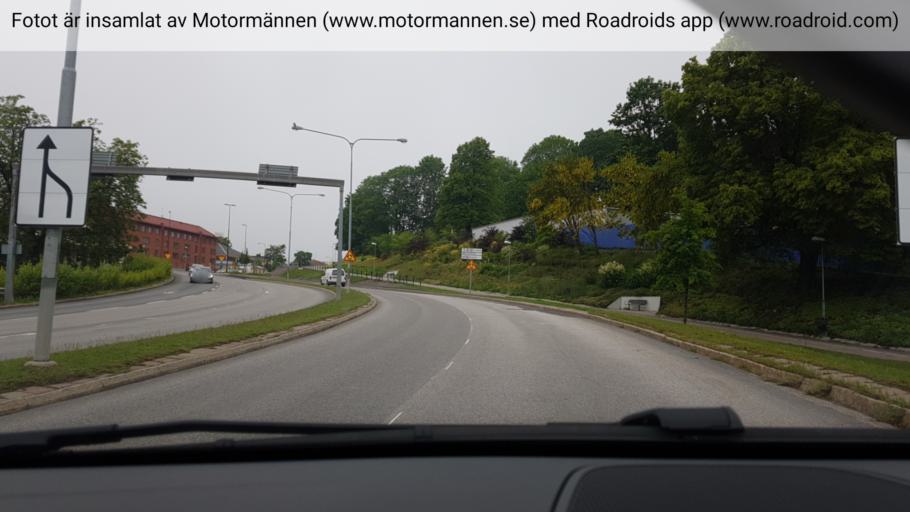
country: SE
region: OEstergoetland
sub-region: Motala Kommun
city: Motala
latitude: 58.5369
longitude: 15.0434
